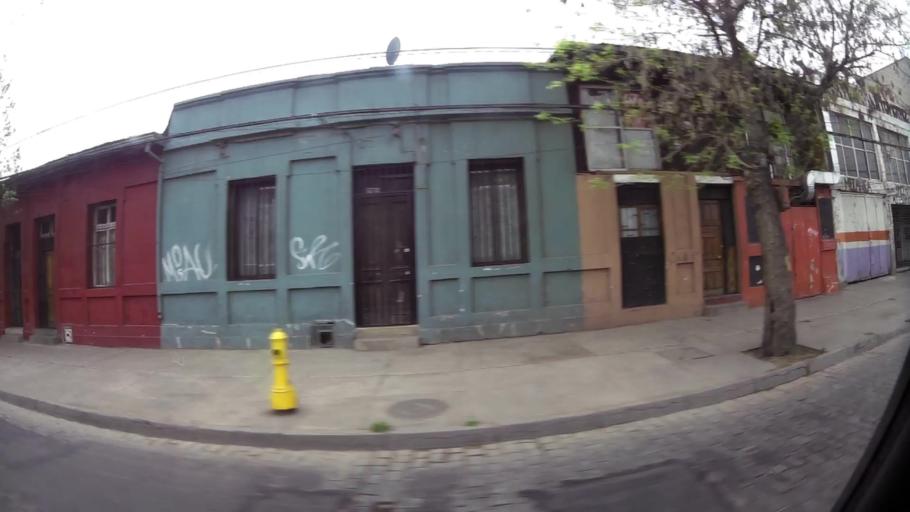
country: CL
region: Santiago Metropolitan
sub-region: Provincia de Santiago
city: Santiago
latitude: -33.4743
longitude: -70.6543
